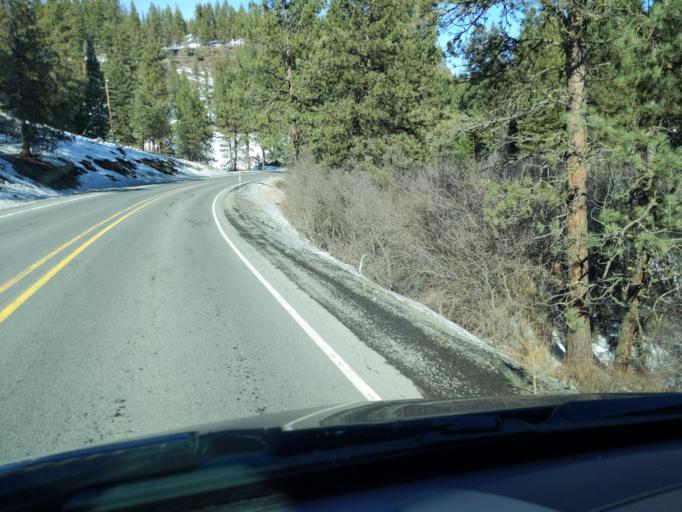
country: US
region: Oregon
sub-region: Grant County
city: John Day
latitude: 44.9383
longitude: -119.0083
